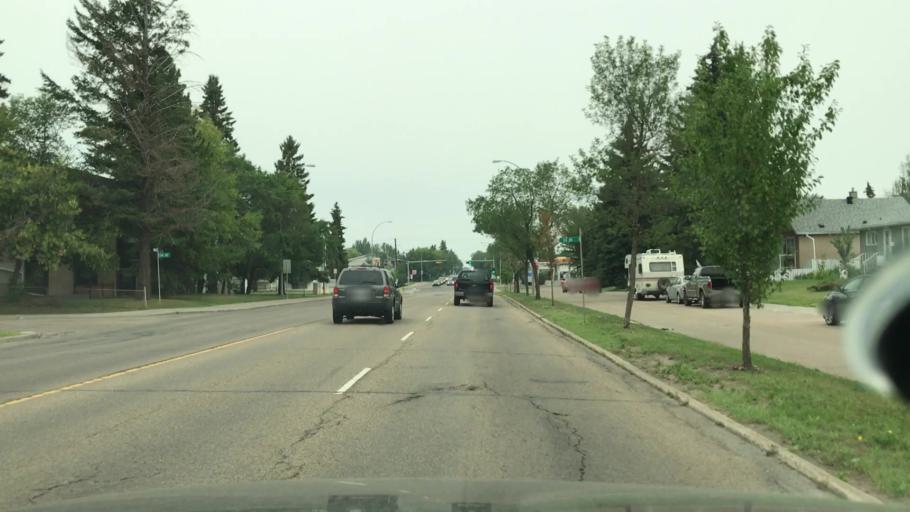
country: CA
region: Alberta
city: Edmonton
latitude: 53.5297
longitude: -113.5779
